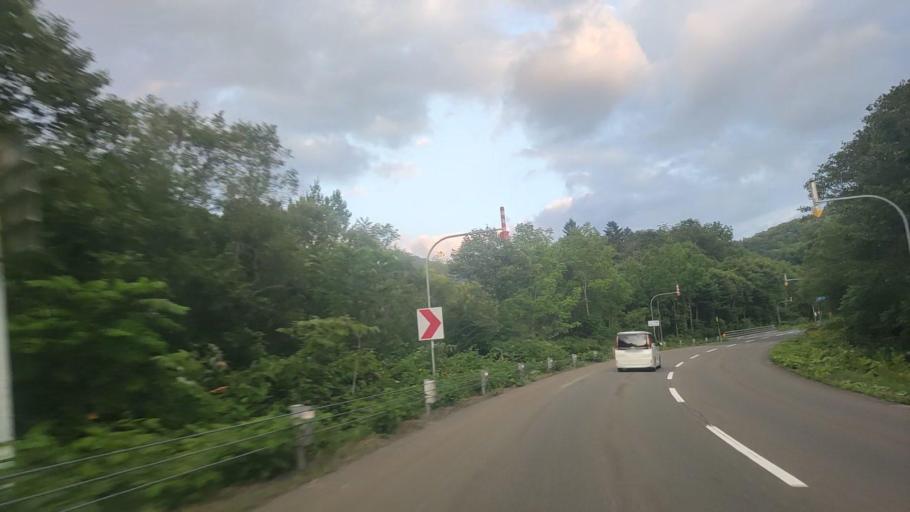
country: JP
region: Hokkaido
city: Ashibetsu
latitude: 43.3684
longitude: 142.2277
